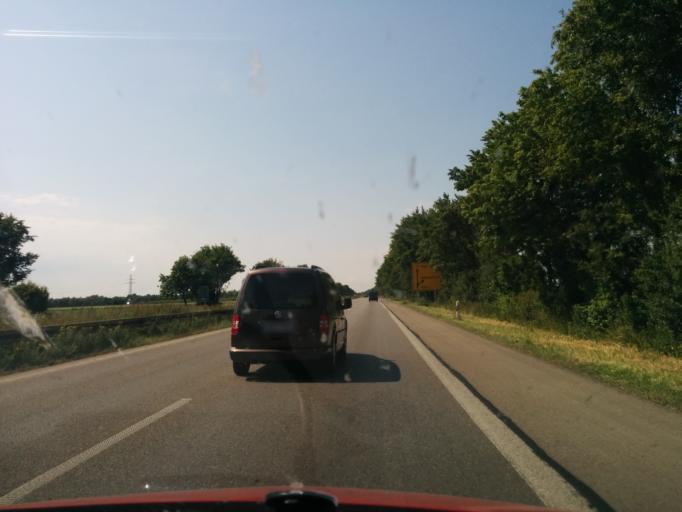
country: DE
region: Bavaria
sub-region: Swabia
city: Konigsbrunn
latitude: 48.2898
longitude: 10.8749
